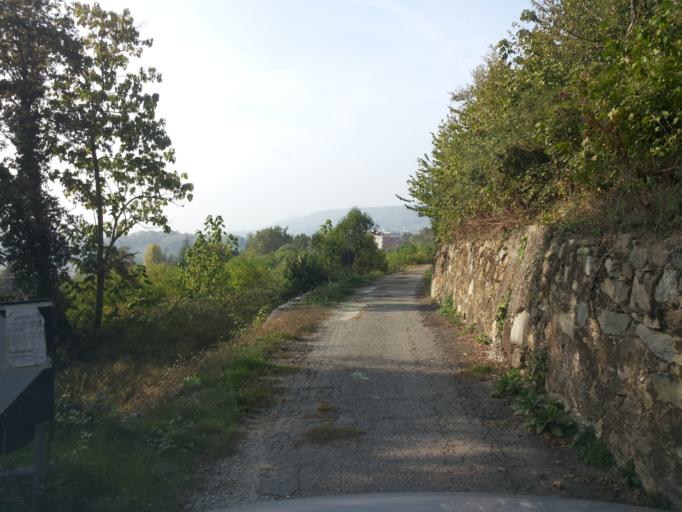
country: IT
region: Piedmont
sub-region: Provincia di Biella
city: Viverone
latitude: 45.4304
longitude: 8.0481
